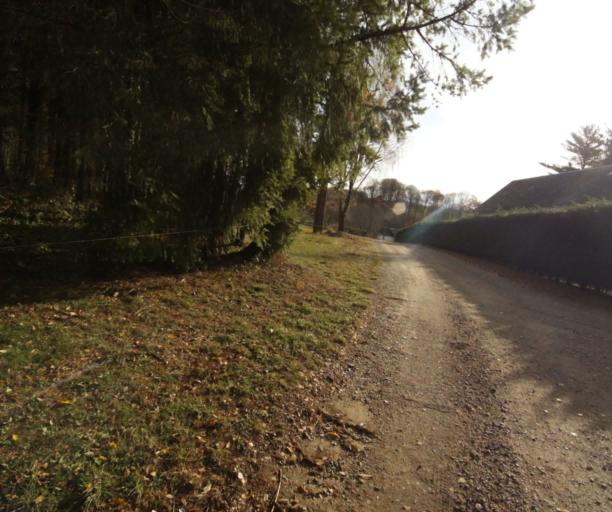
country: FR
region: Limousin
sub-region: Departement de la Correze
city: Cornil
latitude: 45.1948
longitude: 1.7208
